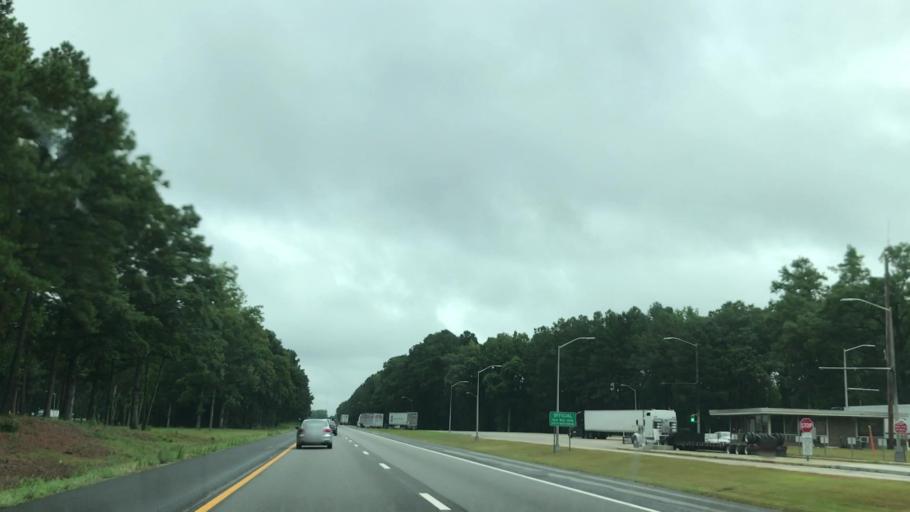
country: US
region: North Carolina
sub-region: Halifax County
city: Enfield
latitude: 36.1469
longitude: -77.7854
